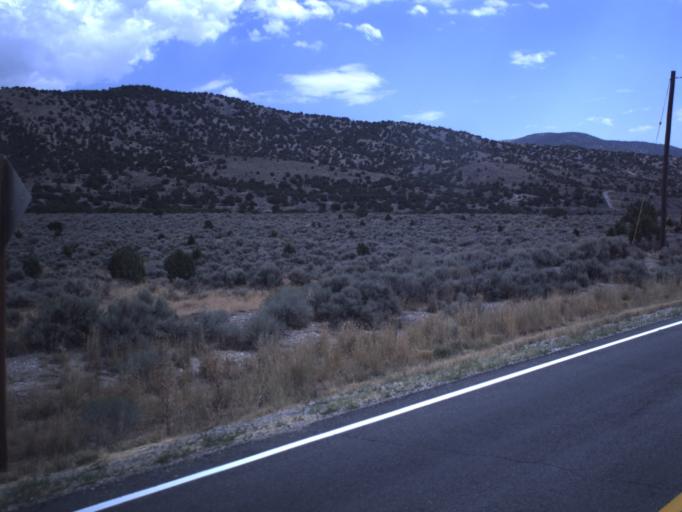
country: US
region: Utah
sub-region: Tooele County
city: Tooele
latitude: 40.3290
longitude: -112.2919
